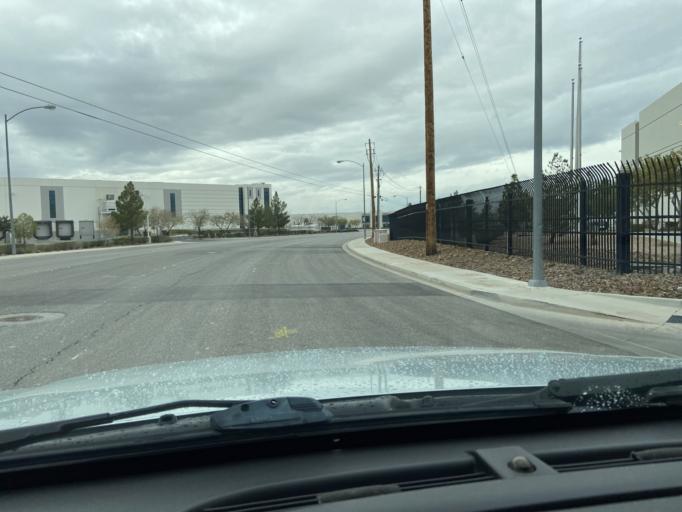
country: US
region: Nevada
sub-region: Clark County
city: Nellis Air Force Base
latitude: 36.2472
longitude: -115.1007
